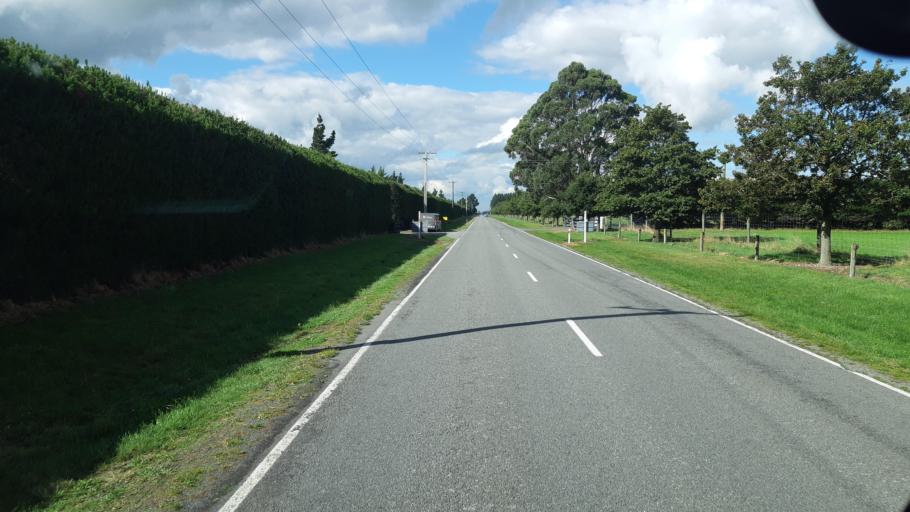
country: NZ
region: Canterbury
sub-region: Waimakariri District
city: Oxford
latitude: -43.3275
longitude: 172.1661
